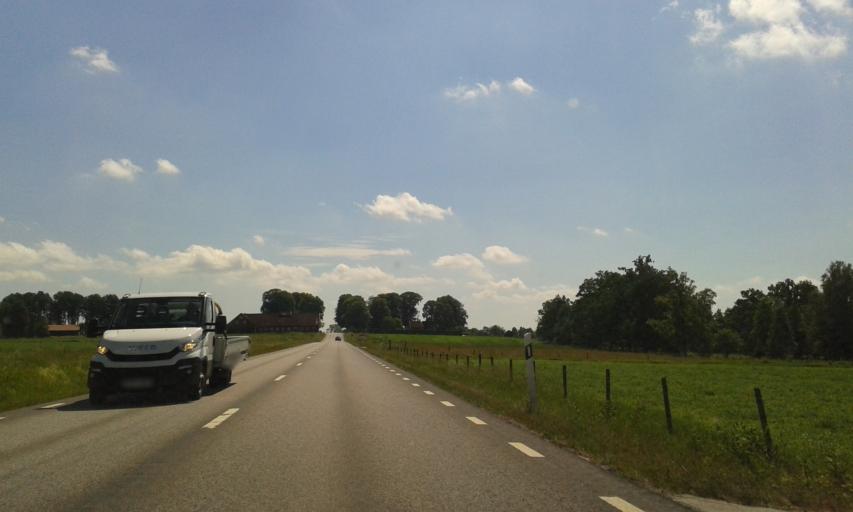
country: SE
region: Kronoberg
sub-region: Vaxjo Kommun
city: Ingelstad
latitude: 56.7742
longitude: 14.9108
